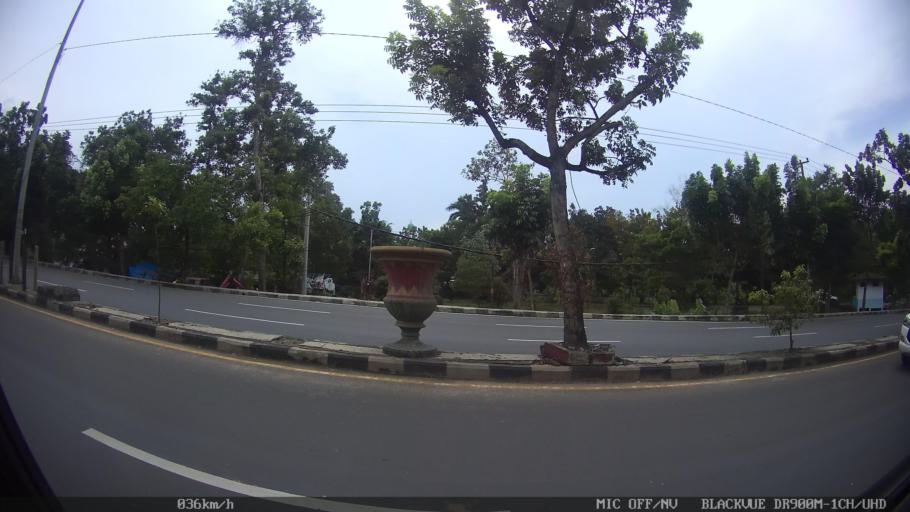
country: ID
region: Lampung
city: Kedaton
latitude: -5.3694
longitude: 105.2372
